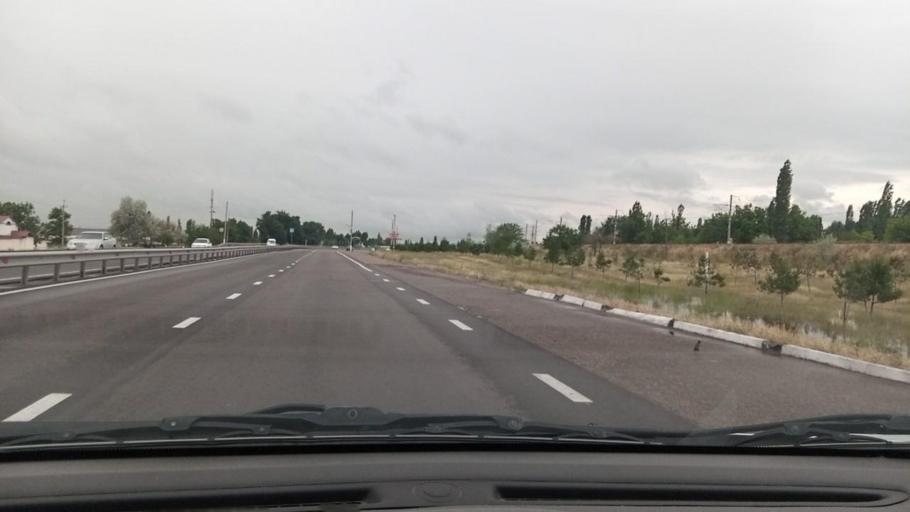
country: UZ
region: Toshkent
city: Ohangaron
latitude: 40.9082
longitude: 69.8005
